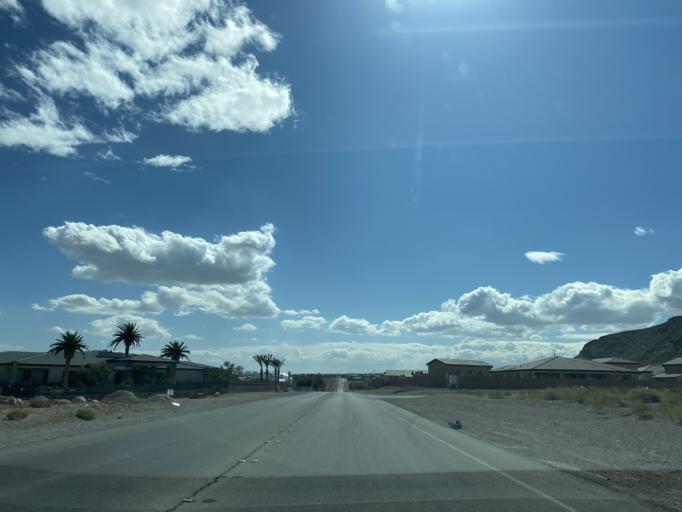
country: US
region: Nevada
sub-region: Clark County
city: Summerlin South
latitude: 36.2450
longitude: -115.3064
